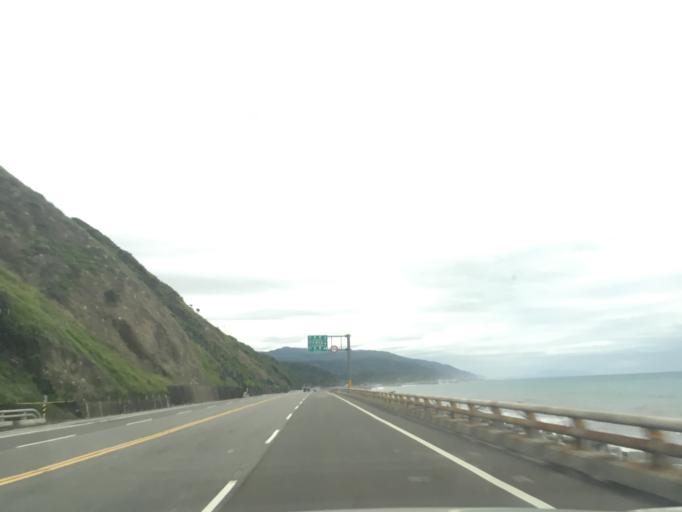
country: TW
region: Taiwan
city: Hengchun
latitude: 22.3140
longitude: 120.8913
